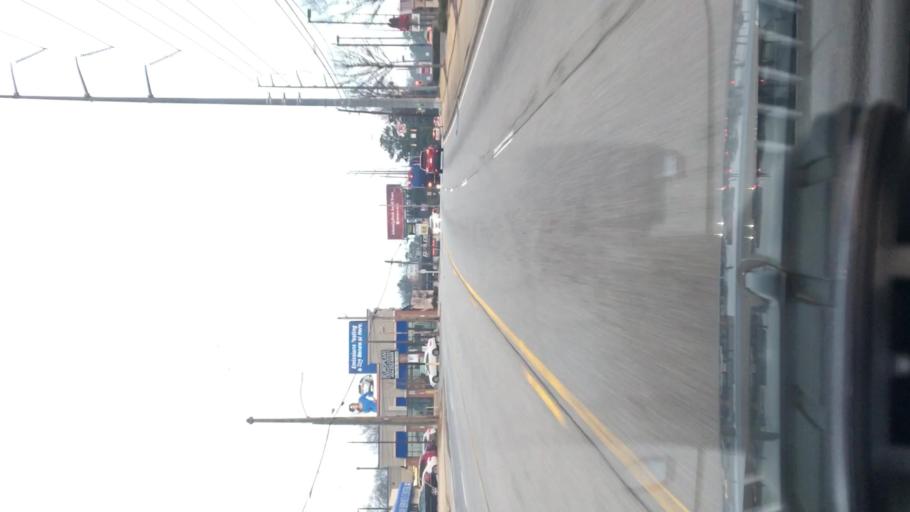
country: US
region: Georgia
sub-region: DeKalb County
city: North Atlanta
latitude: 33.8742
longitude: -84.3810
